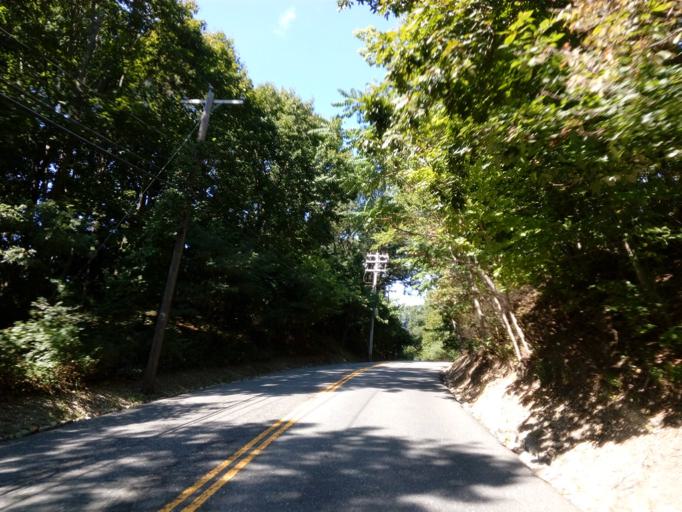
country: US
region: New York
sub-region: Nassau County
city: Laurel Hollow
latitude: 40.8570
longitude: -73.4714
